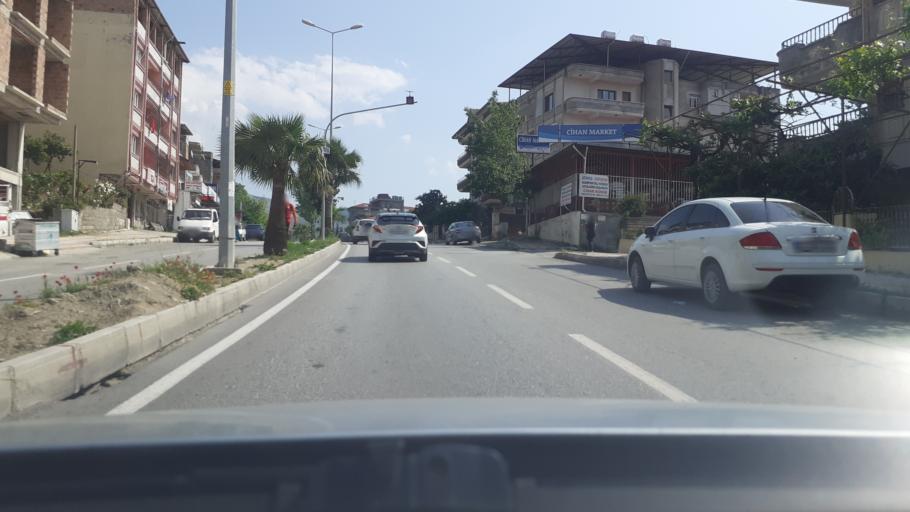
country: TR
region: Hatay
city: Gumusgoze
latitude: 36.1431
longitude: 36.1412
